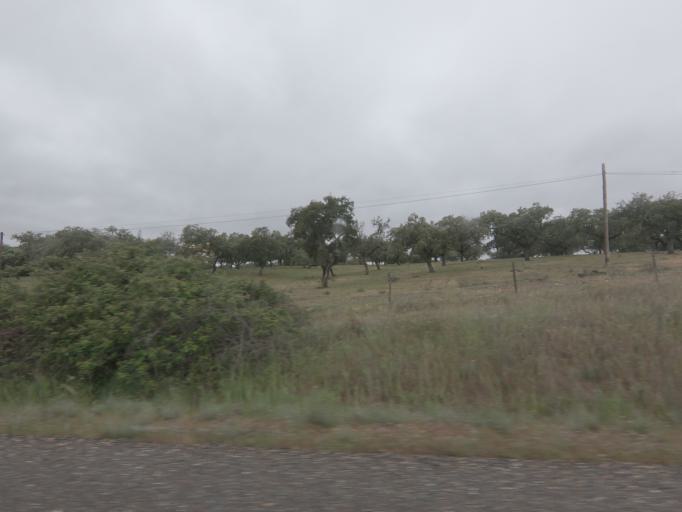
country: ES
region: Extremadura
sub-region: Provincia de Badajoz
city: Puebla de Obando
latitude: 39.1445
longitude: -6.6532
